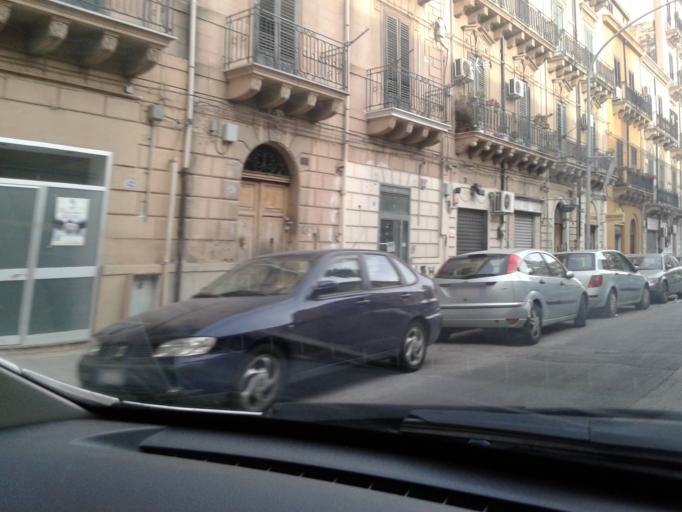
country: IT
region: Sicily
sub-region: Palermo
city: Palermo
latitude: 38.1080
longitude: 13.3405
